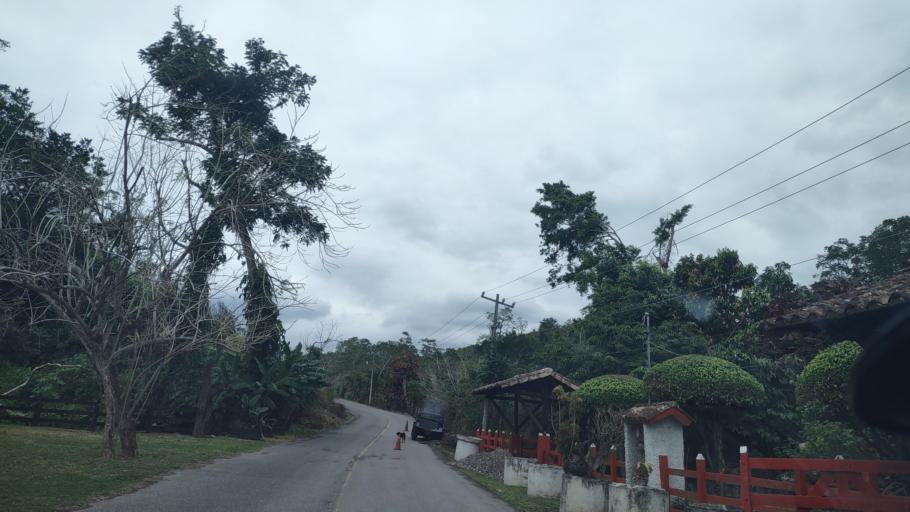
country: MX
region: Veracruz
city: Papantla de Olarte
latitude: 20.4445
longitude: -97.2902
